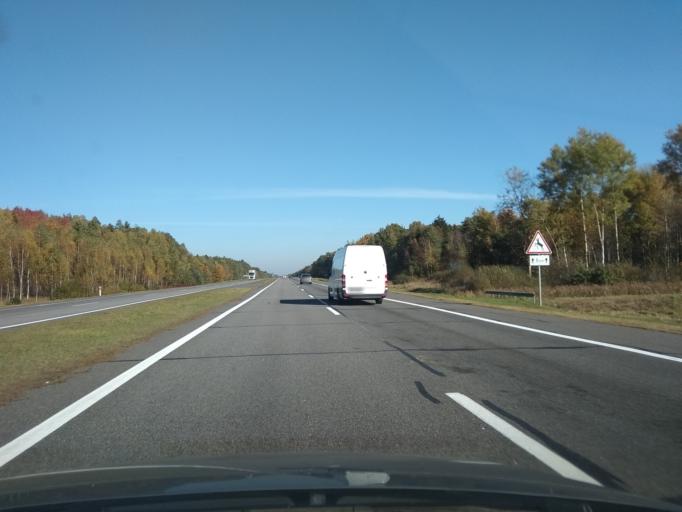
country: BY
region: Brest
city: Ivatsevichy
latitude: 52.7457
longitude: 25.4906
